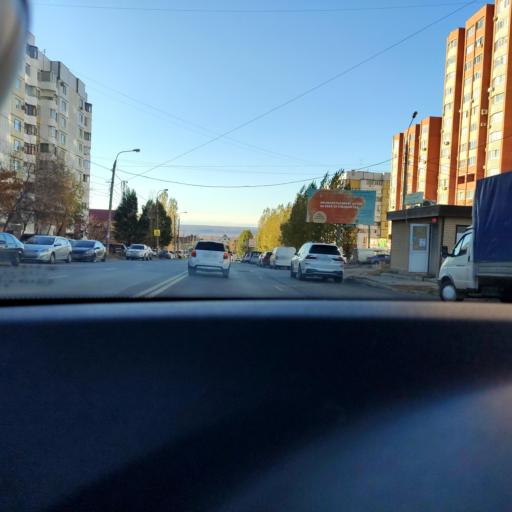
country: RU
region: Samara
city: Samara
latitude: 53.2649
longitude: 50.2169
